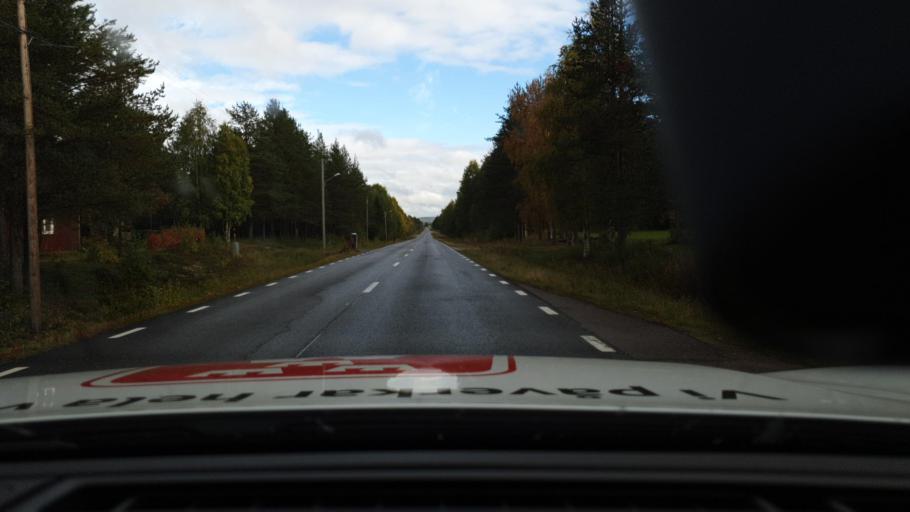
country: SE
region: Norrbotten
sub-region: Overkalix Kommun
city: OEverkalix
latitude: 66.9500
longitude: 22.7105
